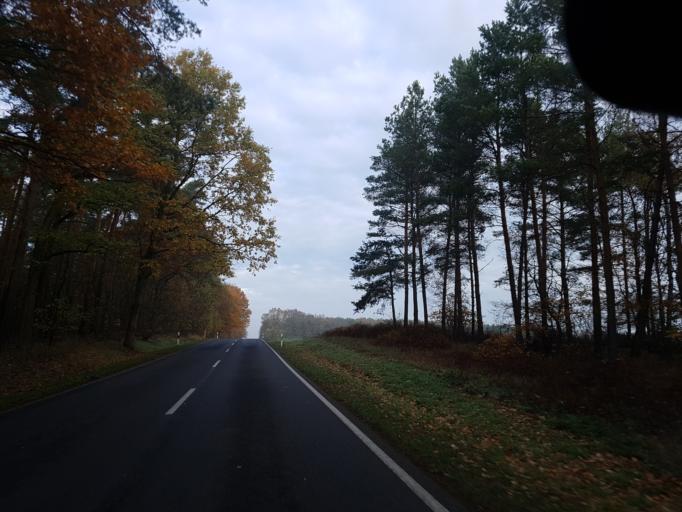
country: DE
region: Saxony-Anhalt
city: Kropstadt
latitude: 51.9529
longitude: 12.7501
